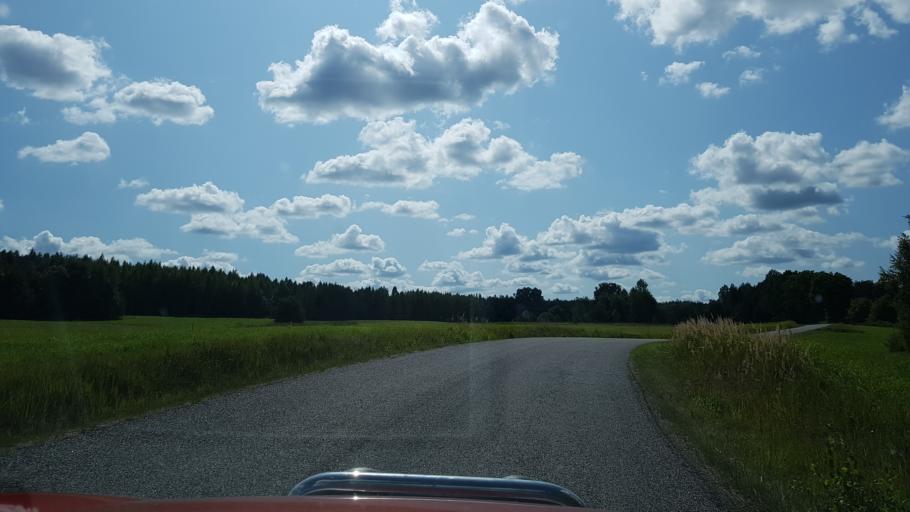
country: EE
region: Vorumaa
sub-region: Voru linn
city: Voru
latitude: 57.7244
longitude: 27.2108
